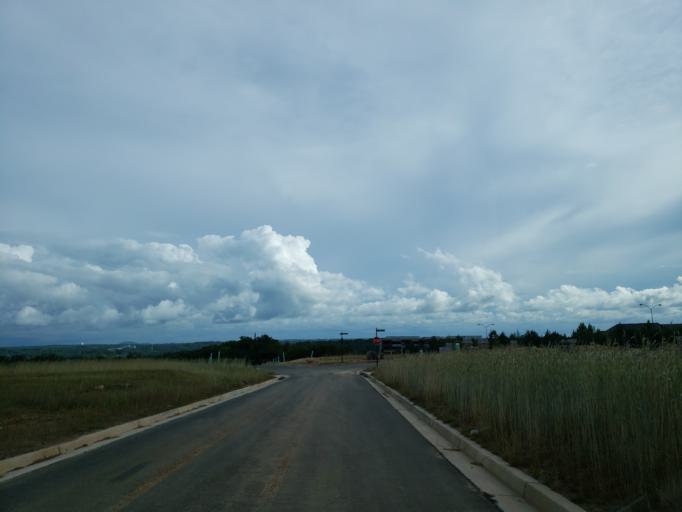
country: US
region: Georgia
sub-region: Cherokee County
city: Canton
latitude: 34.2740
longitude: -84.4695
